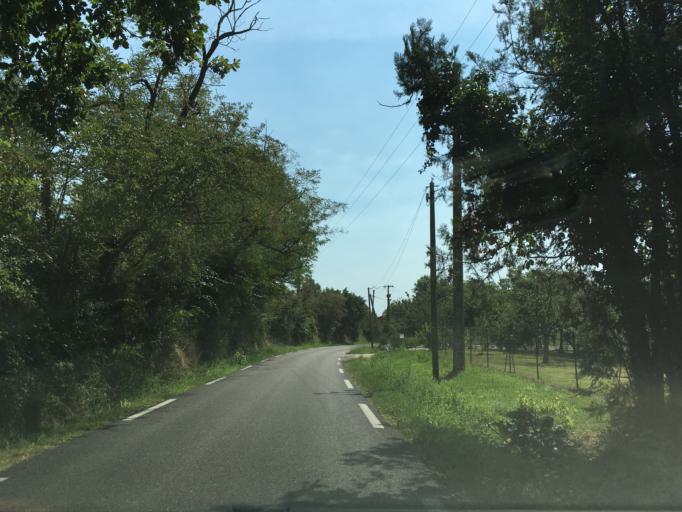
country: FR
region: Midi-Pyrenees
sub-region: Departement du Tarn-et-Garonne
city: Saint-Nauphary
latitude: 43.9724
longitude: 1.3957
